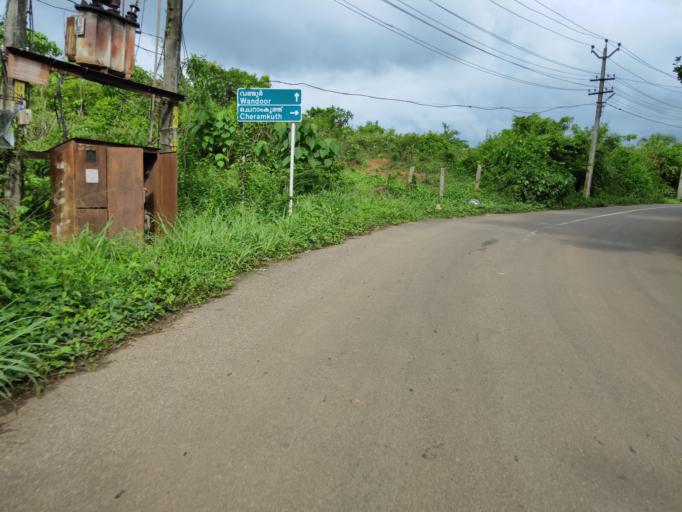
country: IN
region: Kerala
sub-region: Malappuram
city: Manjeri
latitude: 11.1443
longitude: 76.1393
